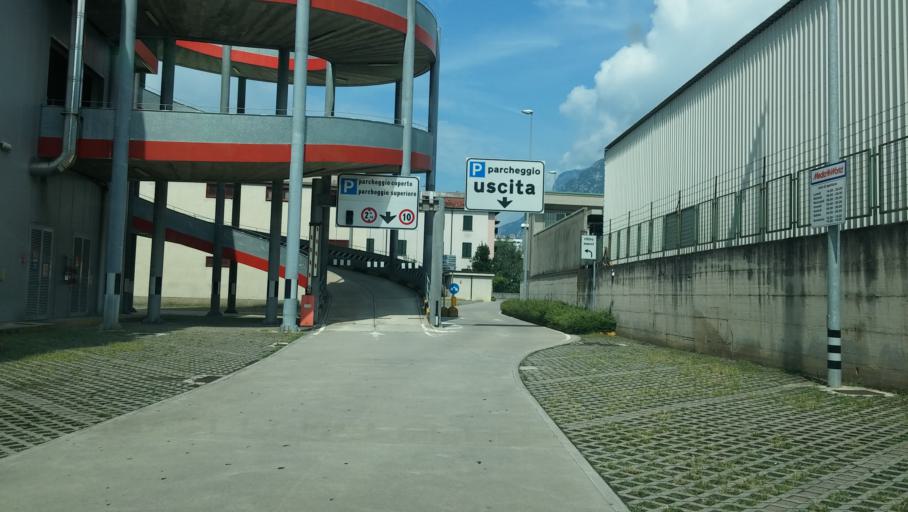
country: IT
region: Lombardy
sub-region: Provincia di Lecco
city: Pescate
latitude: 45.8405
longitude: 9.4025
